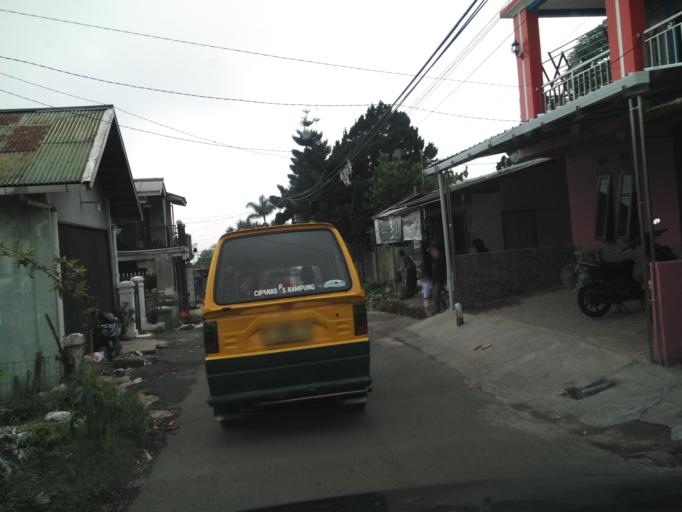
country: ID
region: West Java
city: Sukabumi
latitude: -6.7470
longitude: 107.0364
